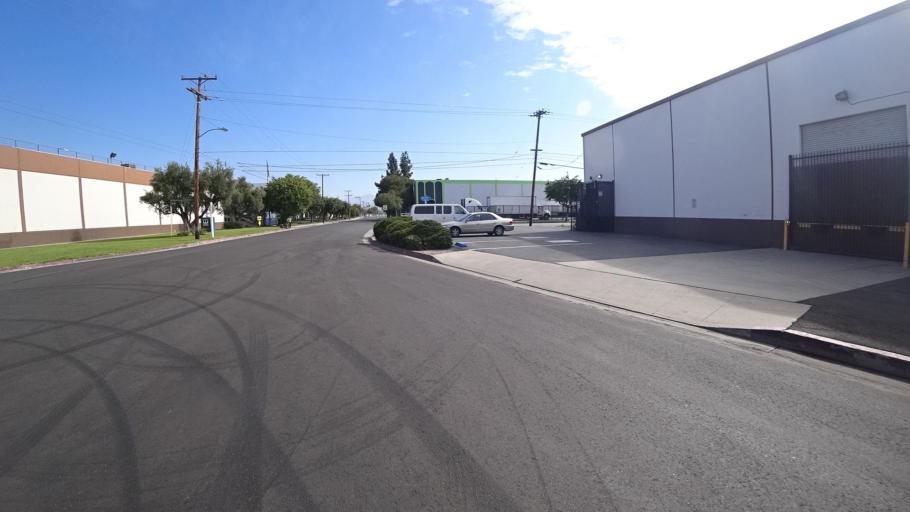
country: US
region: California
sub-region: Los Angeles County
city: La Puente
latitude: 34.0283
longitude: -117.9642
